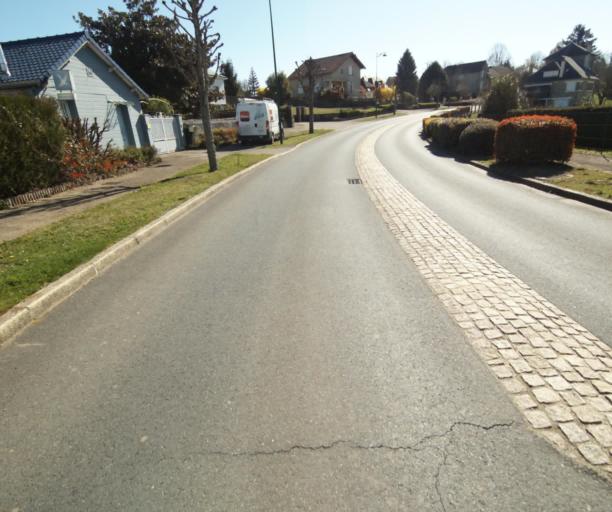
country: FR
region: Limousin
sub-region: Departement de la Correze
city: Seilhac
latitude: 45.3654
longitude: 1.7226
